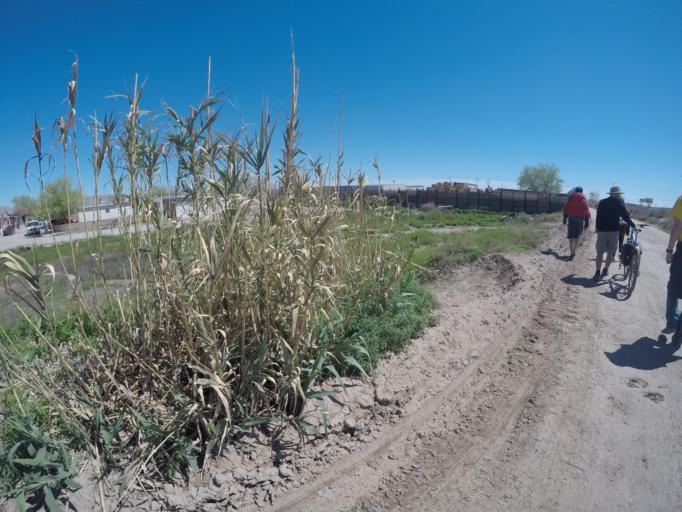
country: US
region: Texas
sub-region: El Paso County
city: Socorro Mission Number 1 Colonia
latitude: 31.6070
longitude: -106.3115
